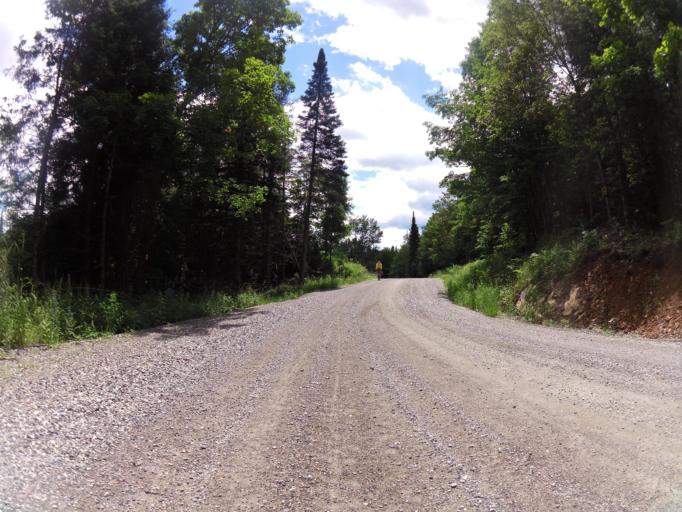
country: CA
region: Ontario
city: Renfrew
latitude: 45.0400
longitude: -76.7424
